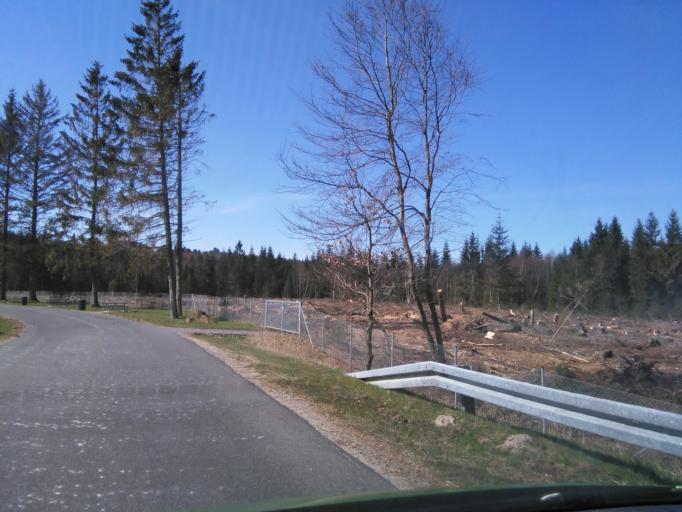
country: DK
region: Central Jutland
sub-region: Hedensted Kommune
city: Torring
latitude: 55.9922
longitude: 9.4642
